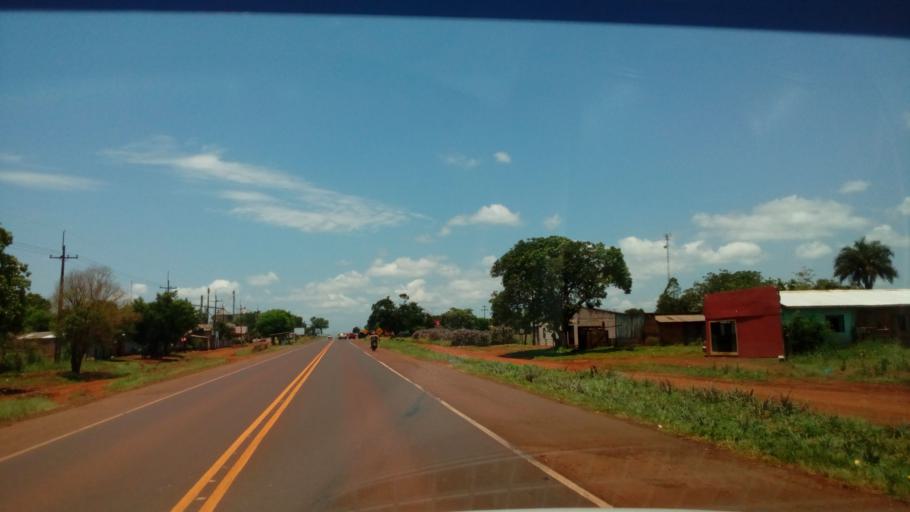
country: PY
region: Alto Parana
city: Naranjal
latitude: -25.9308
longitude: -55.1155
